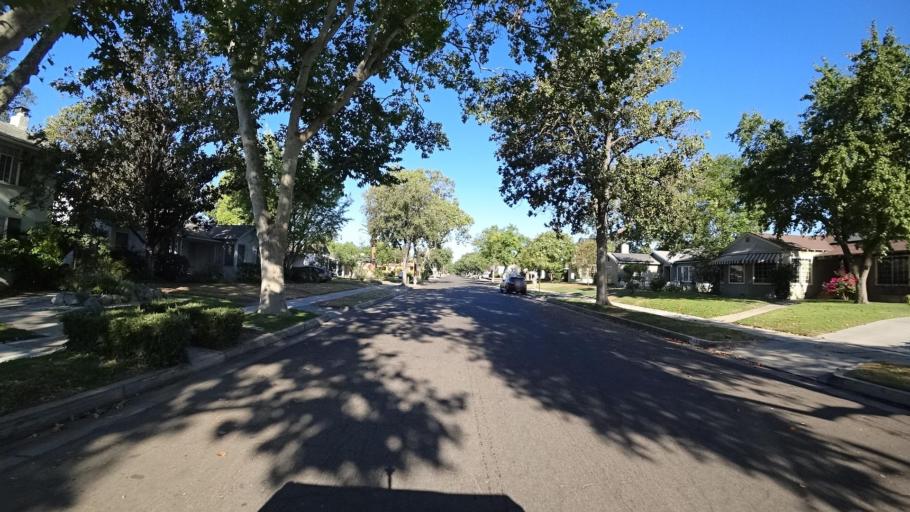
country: US
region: California
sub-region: Fresno County
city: Fresno
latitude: 36.7667
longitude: -119.8100
